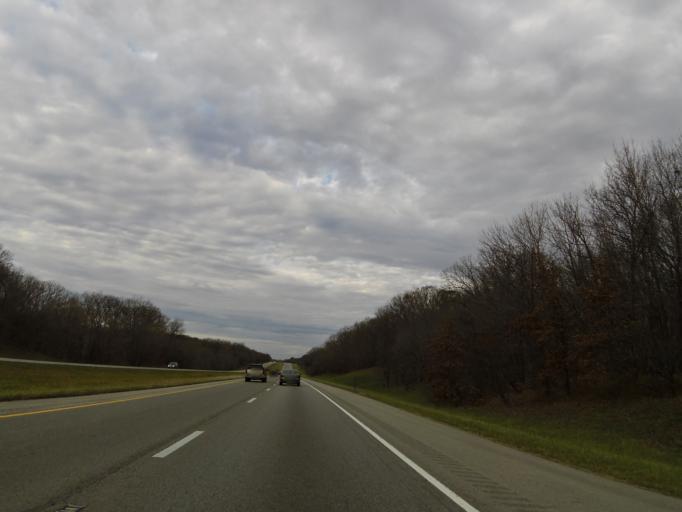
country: US
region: Illinois
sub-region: Clinton County
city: Wamac
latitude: 38.3788
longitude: -89.1086
